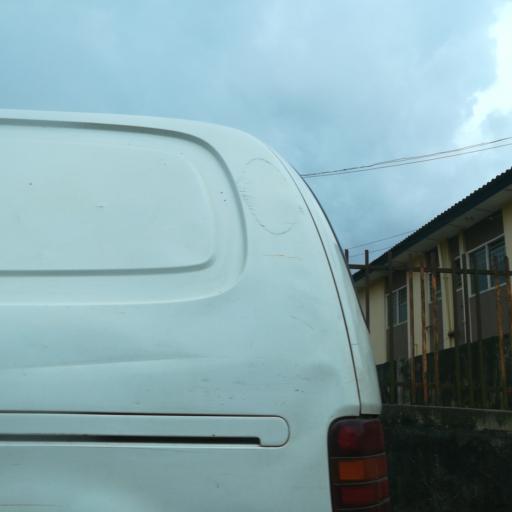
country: NG
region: Lagos
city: Agege
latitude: 6.6057
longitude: 3.2950
